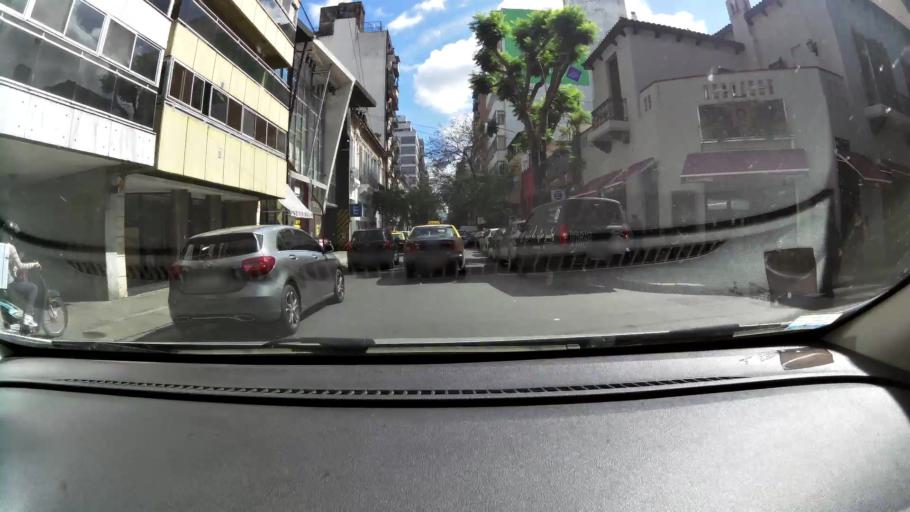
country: AR
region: Santa Fe
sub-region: Departamento de Rosario
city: Rosario
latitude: -32.9449
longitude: -60.6450
